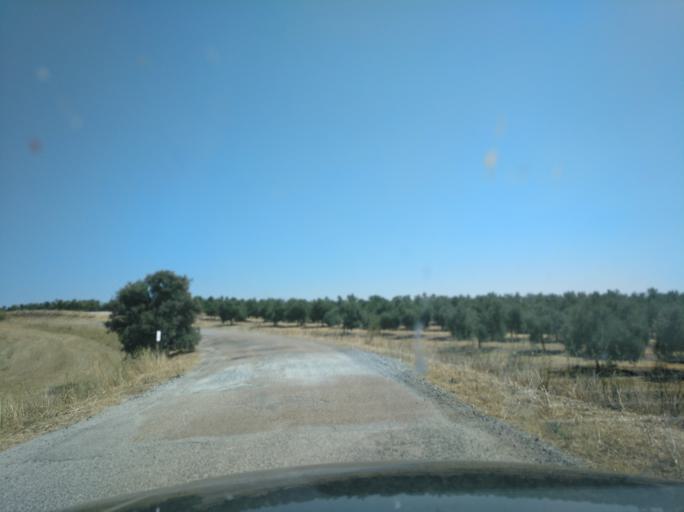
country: PT
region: Portalegre
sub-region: Campo Maior
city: Campo Maior
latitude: 38.9833
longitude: -7.0981
